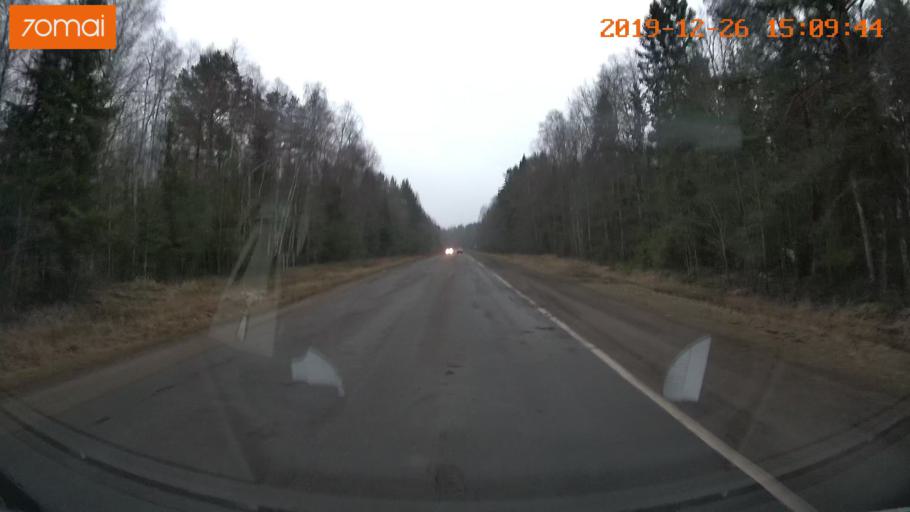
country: RU
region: Jaroslavl
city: Rybinsk
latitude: 58.1464
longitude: 38.8438
